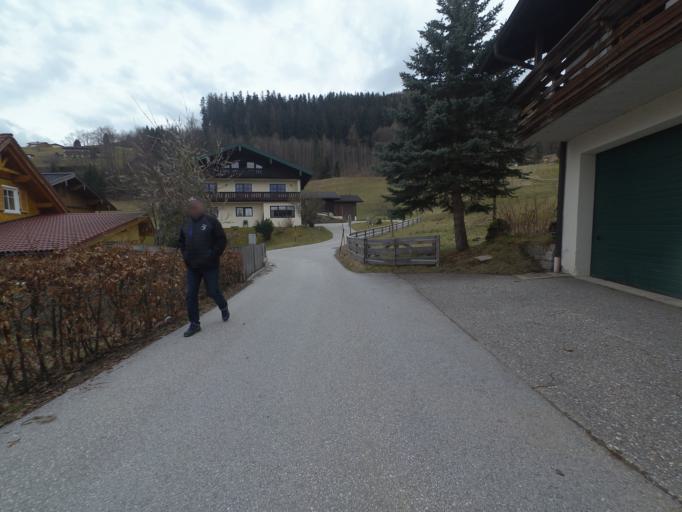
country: AT
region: Salzburg
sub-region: Politischer Bezirk Hallein
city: Hallein
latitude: 47.6592
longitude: 13.0926
